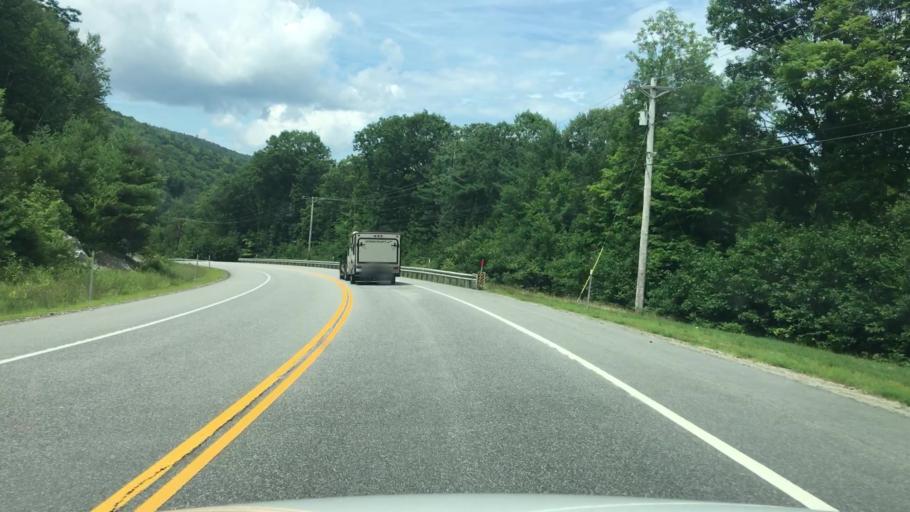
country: US
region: New Hampshire
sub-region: Grafton County
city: Rumney
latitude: 43.8421
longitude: -71.9040
